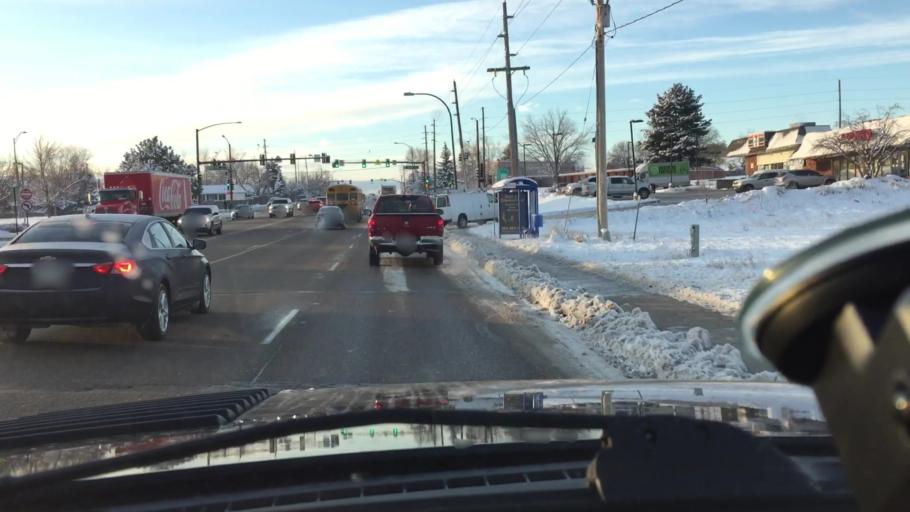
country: US
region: Colorado
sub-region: Adams County
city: Federal Heights
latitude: 39.8574
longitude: -104.9967
